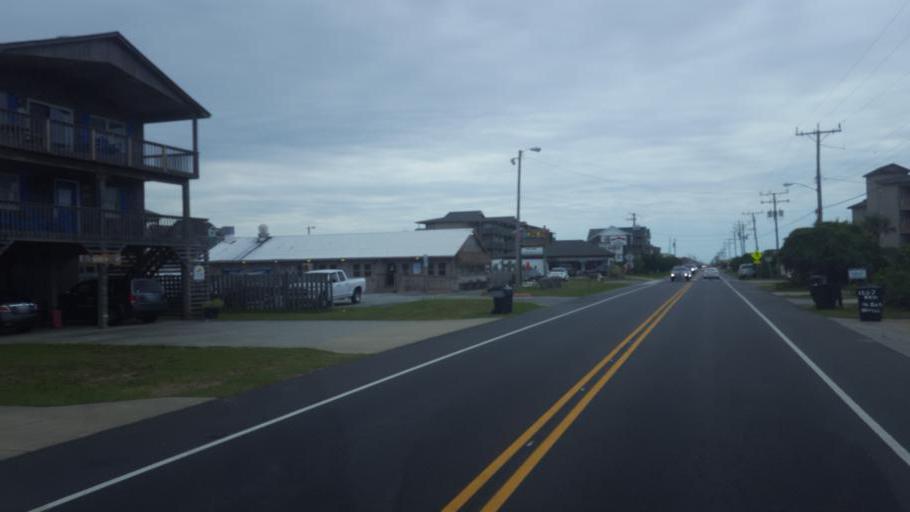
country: US
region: North Carolina
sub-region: Dare County
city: Kill Devil Hills
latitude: 36.0053
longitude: -75.6521
